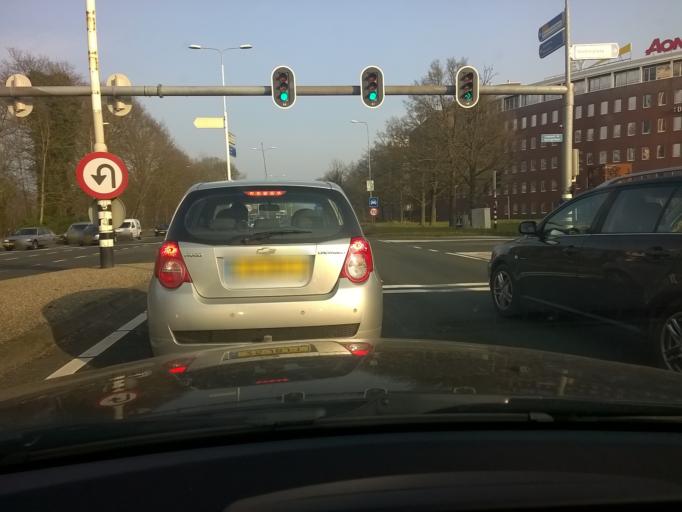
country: NL
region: Groningen
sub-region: Gemeente Groningen
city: Groningen
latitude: 53.2021
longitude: 6.5527
